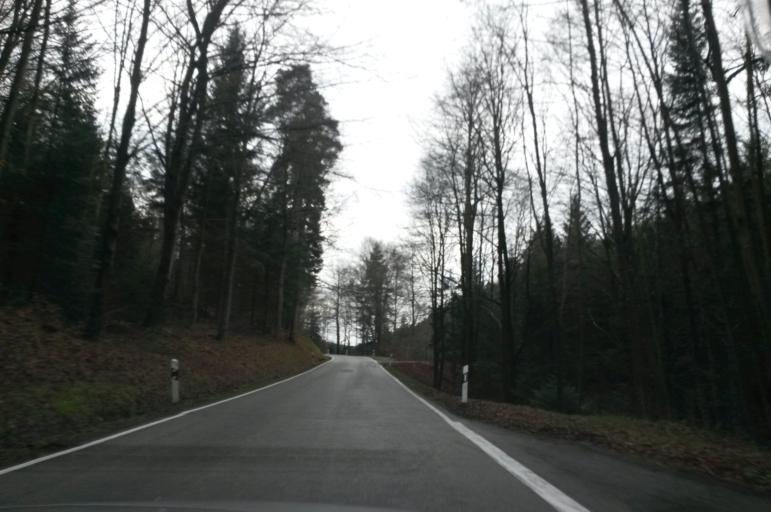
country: DE
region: Baden-Wuerttemberg
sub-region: Karlsruhe Region
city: Engelsbrand
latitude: 48.8375
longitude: 8.6260
